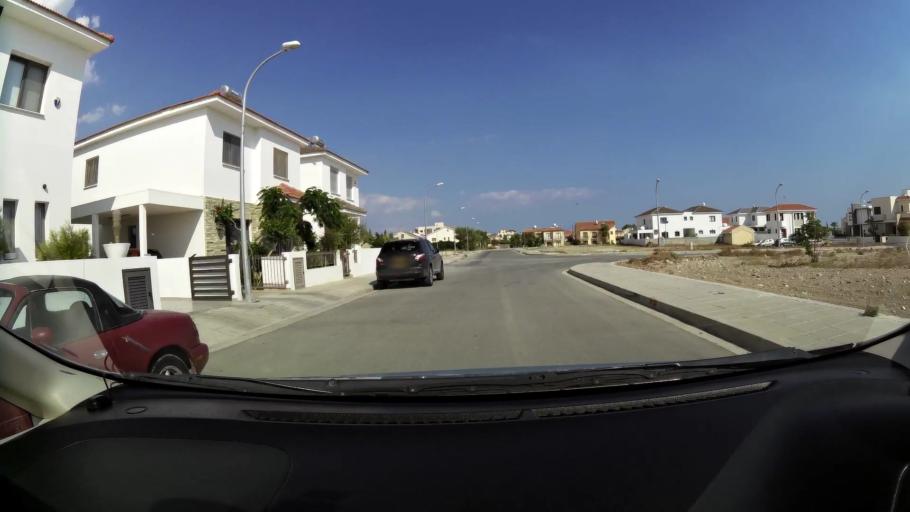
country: CY
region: Larnaka
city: Dhromolaxia
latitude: 34.9048
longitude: 33.5817
